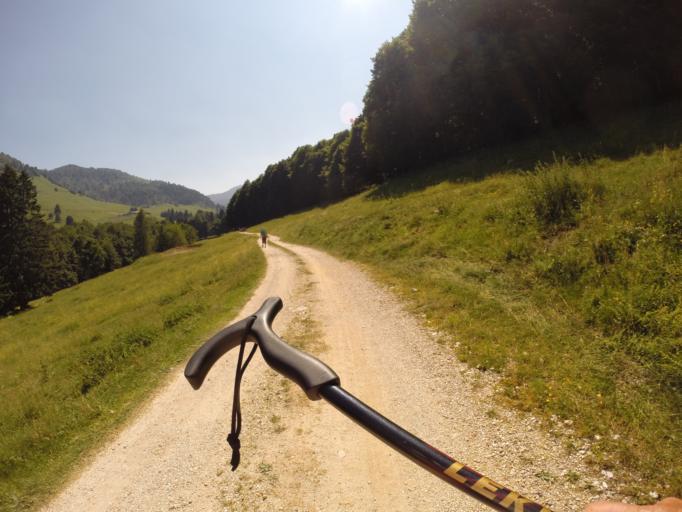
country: IT
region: Veneto
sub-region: Provincia di Treviso
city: Crespano del Grappa
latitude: 45.8988
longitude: 11.8282
